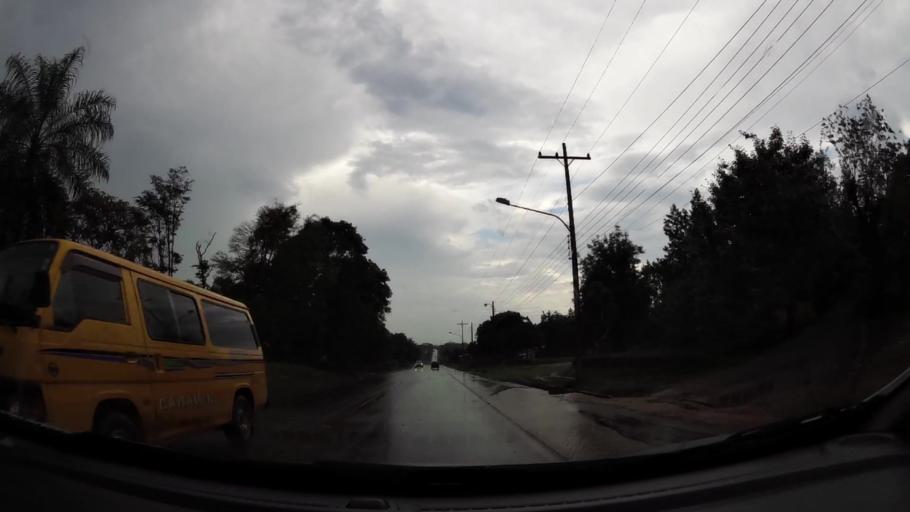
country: PY
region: Alto Parana
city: Presidente Franco
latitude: -25.5590
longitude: -54.6617
